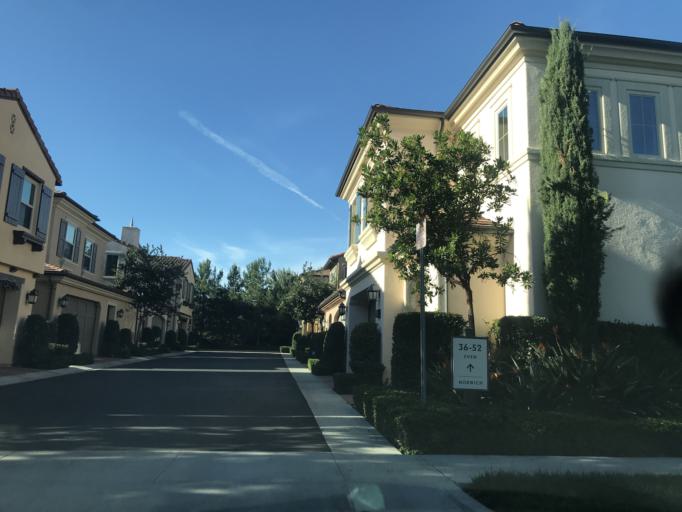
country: US
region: California
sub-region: Orange County
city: Lake Forest
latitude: 33.7038
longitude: -117.7395
